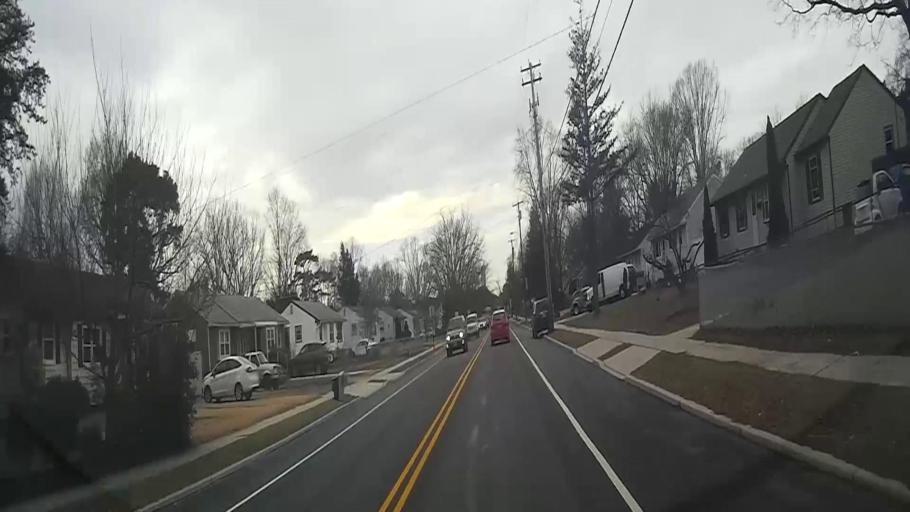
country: US
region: New Jersey
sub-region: Camden County
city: Pine Hill
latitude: 39.7773
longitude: -74.9736
